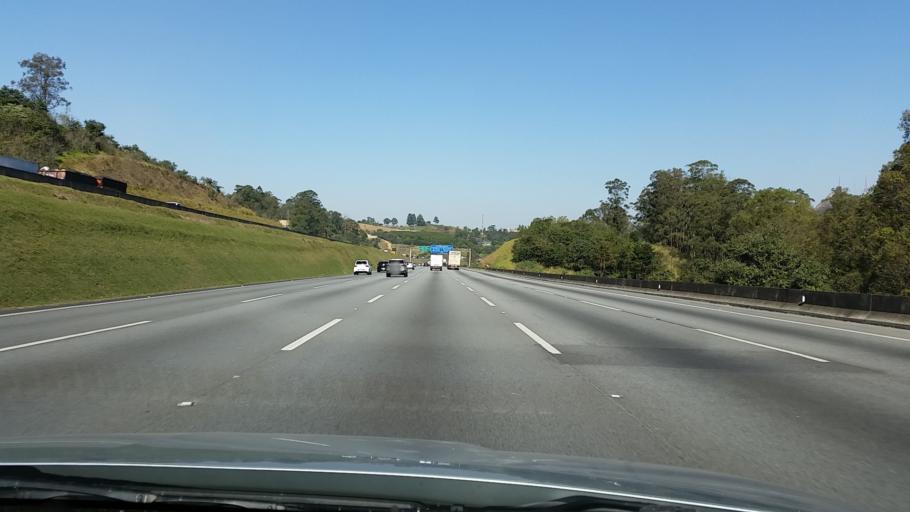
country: BR
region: Sao Paulo
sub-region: Caieiras
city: Caieiras
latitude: -23.4155
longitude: -46.7655
